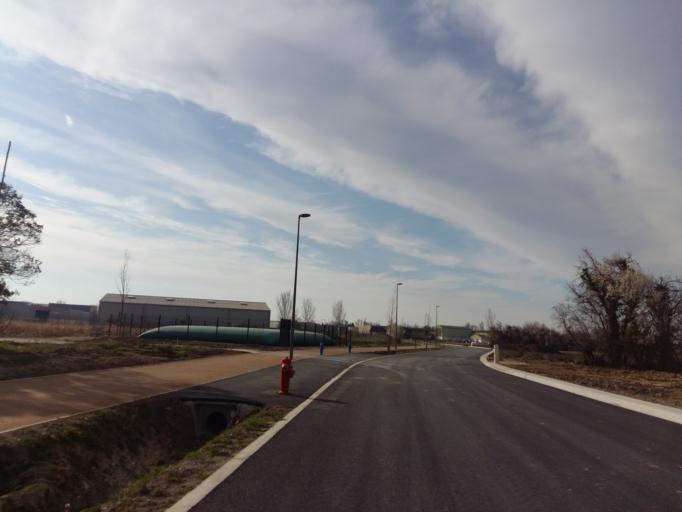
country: FR
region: Provence-Alpes-Cote d'Azur
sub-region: Departement du Vaucluse
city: Le Thor
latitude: 43.9263
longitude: 5.0167
